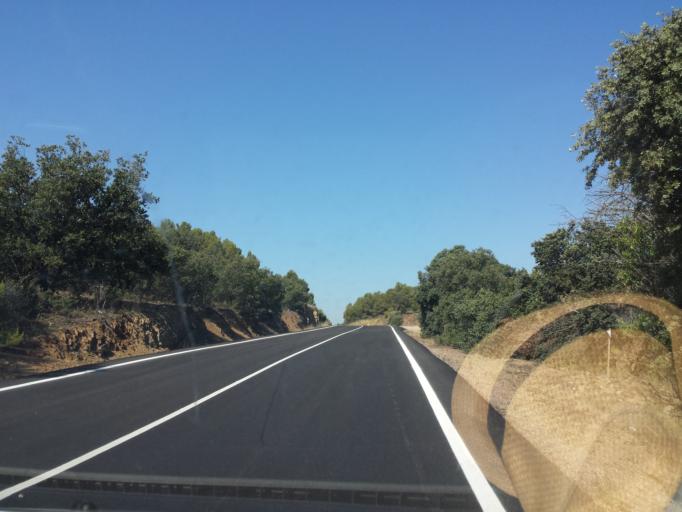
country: ES
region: Aragon
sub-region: Provincia de Zaragoza
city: Munebrega
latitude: 41.2249
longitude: -1.7335
